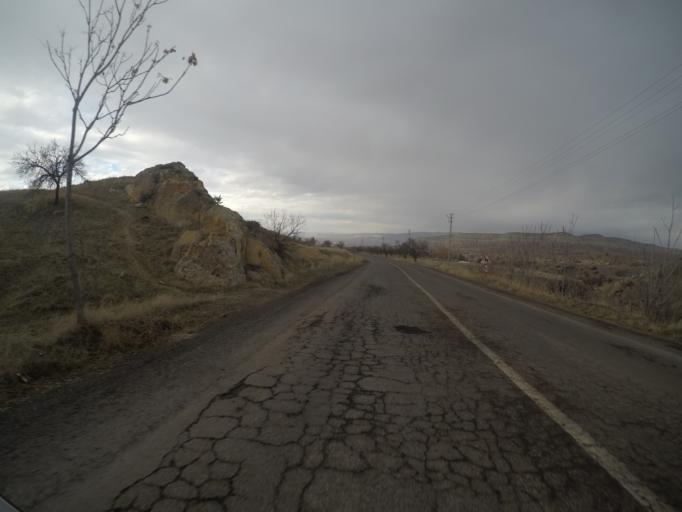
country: TR
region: Nevsehir
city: Goereme
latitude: 38.6346
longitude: 34.8566
